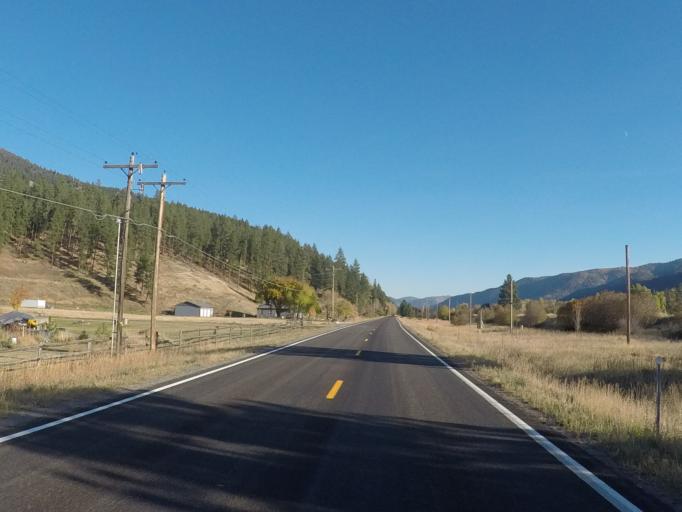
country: US
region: Montana
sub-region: Missoula County
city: Bonner-West Riverside
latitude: 46.8341
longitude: -113.8230
